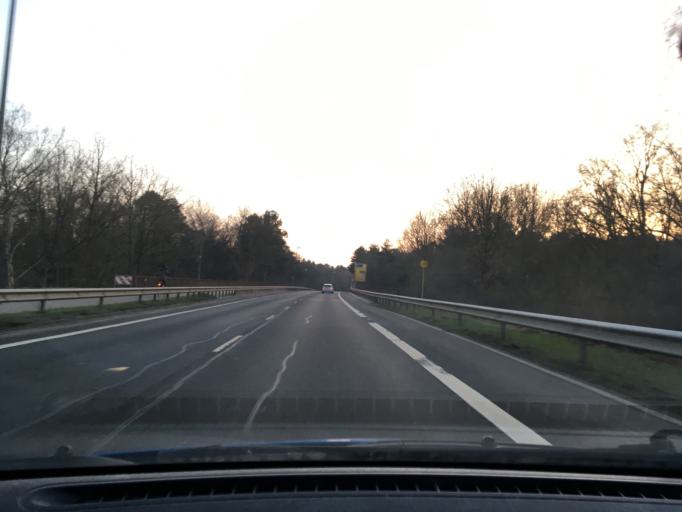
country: DE
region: Lower Saxony
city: Celle
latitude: 52.6213
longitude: 10.0447
